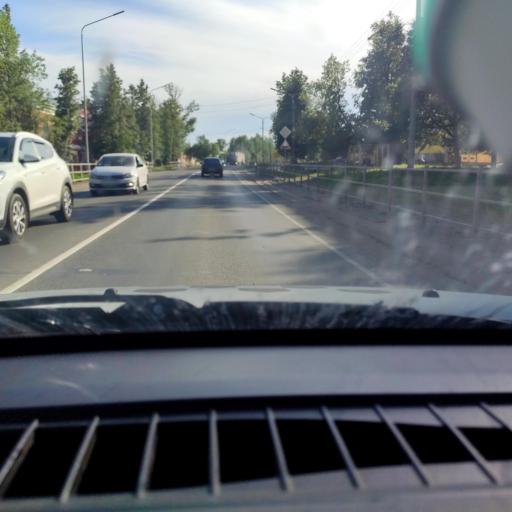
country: RU
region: Kirov
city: Vakhrushi
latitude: 58.6809
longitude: 50.0288
